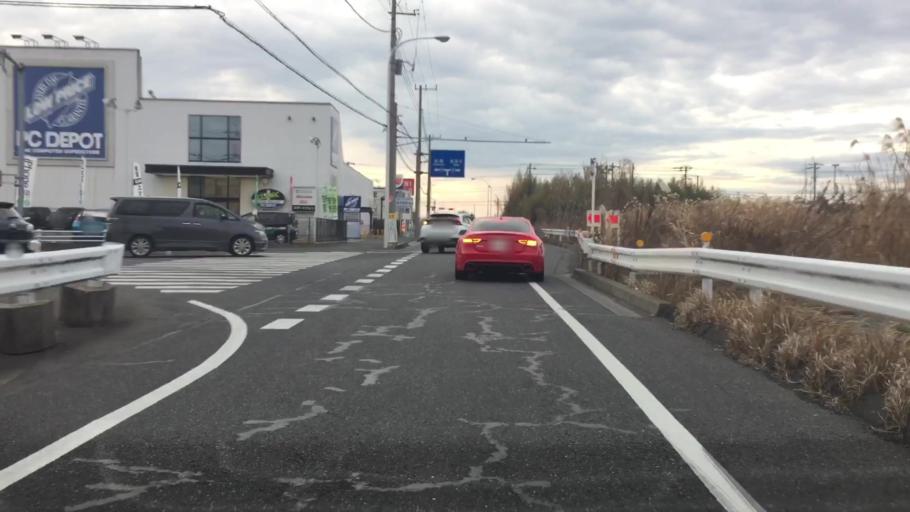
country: JP
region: Chiba
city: Shiroi
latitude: 35.7838
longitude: 140.0045
